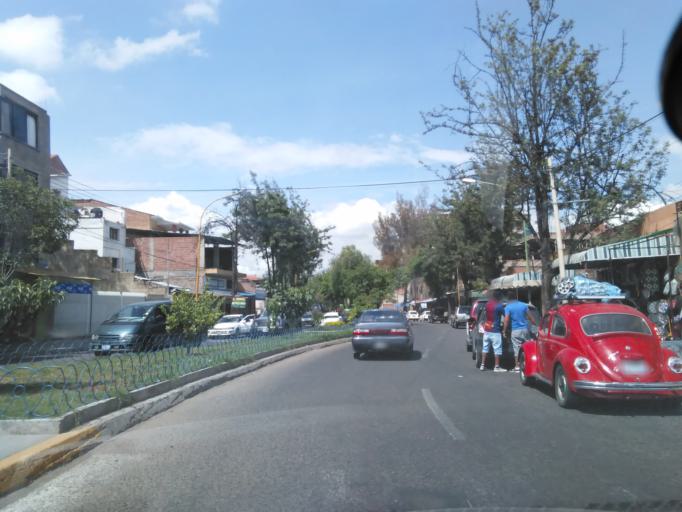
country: BO
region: Cochabamba
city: Cochabamba
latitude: -17.4004
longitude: -66.1626
